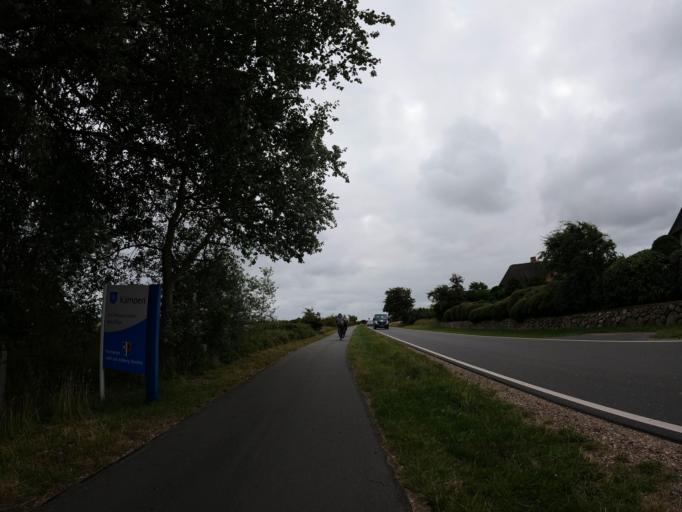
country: DE
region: Schleswig-Holstein
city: Tinnum
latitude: 54.9495
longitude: 8.3461
